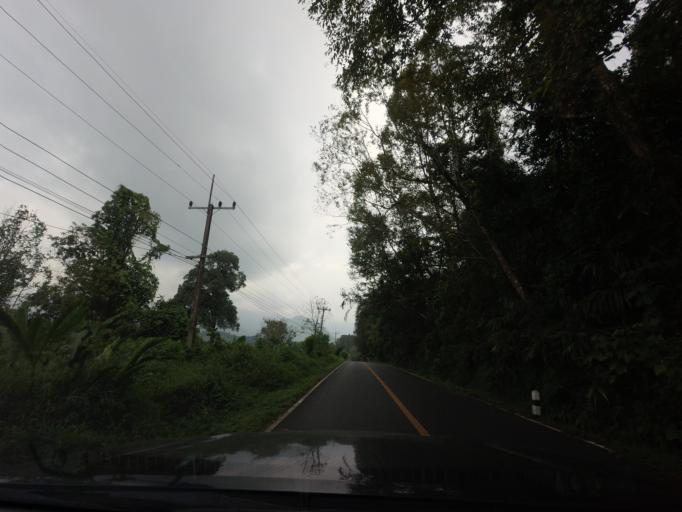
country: TH
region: Nan
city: Pua
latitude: 19.1892
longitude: 101.0304
